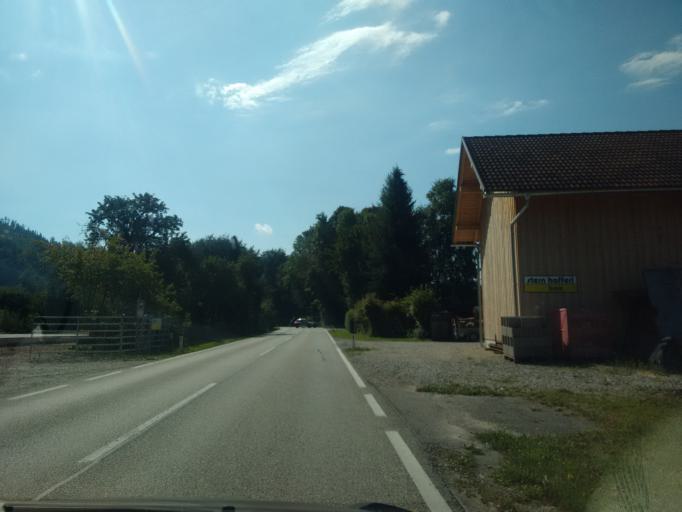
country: AT
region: Upper Austria
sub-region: Politischer Bezirk Gmunden
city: Gruenau im Almtal
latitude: 47.8790
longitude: 13.9408
